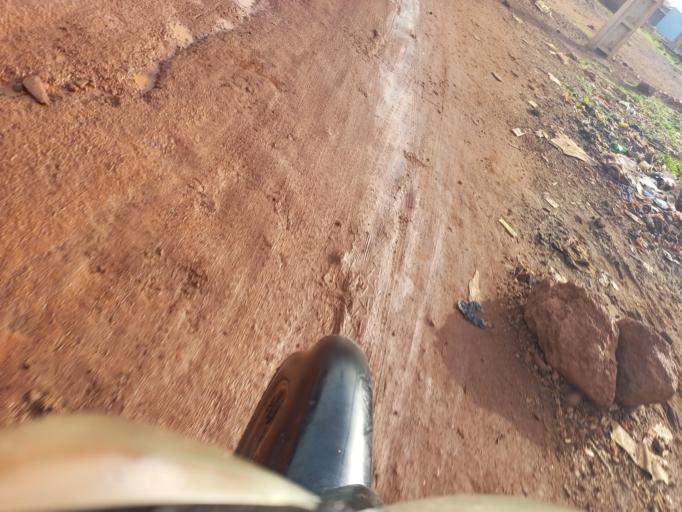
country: ML
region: Bamako
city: Bamako
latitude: 12.5309
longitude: -7.9945
